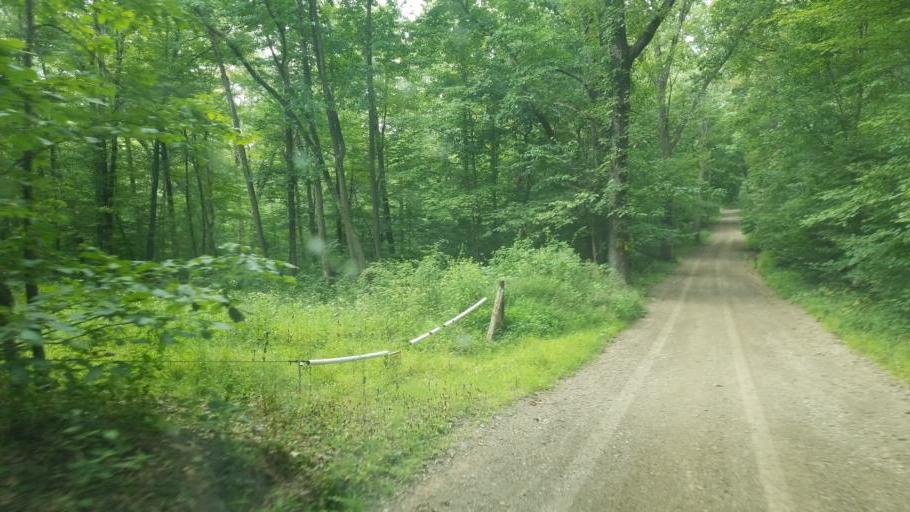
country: US
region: Ohio
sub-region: Ashland County
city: Loudonville
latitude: 40.5726
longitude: -82.2995
